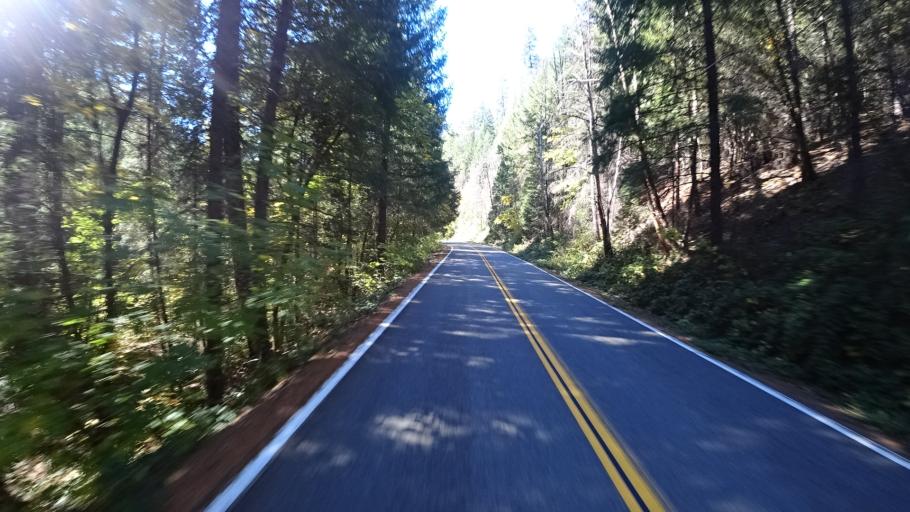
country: US
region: California
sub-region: Trinity County
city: Weaverville
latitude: 41.1920
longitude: -123.0739
